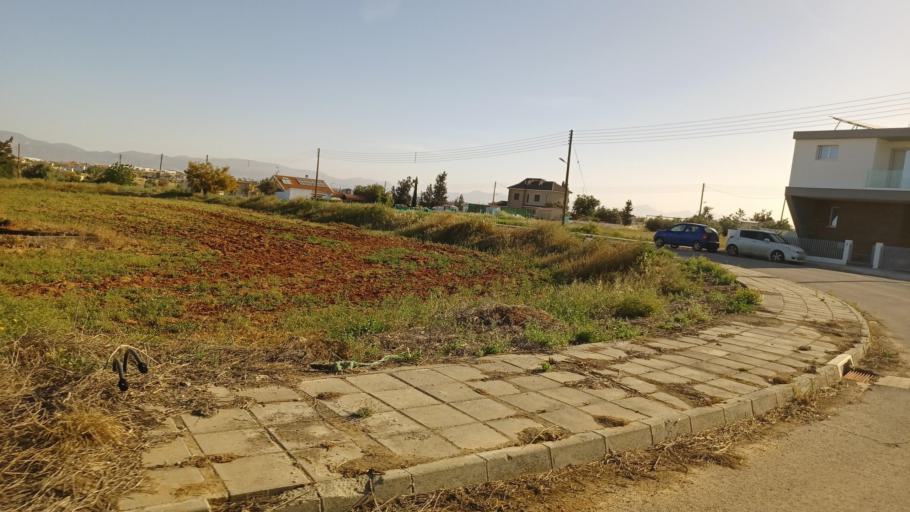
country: CY
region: Lefkosia
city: Kokkinotrimithia
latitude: 35.1492
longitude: 33.1893
